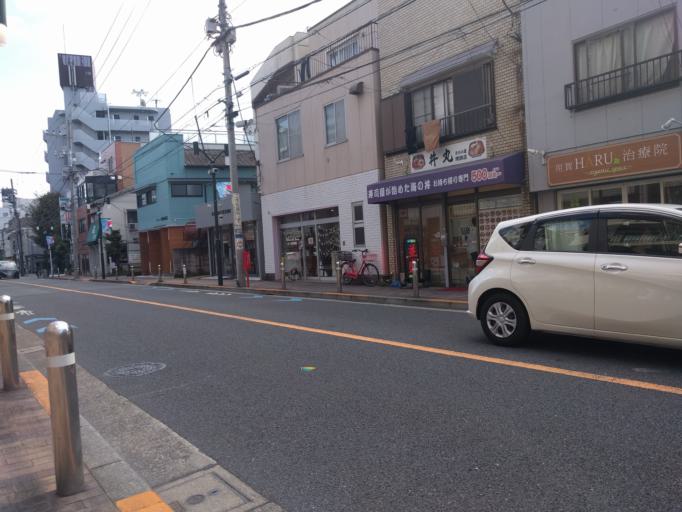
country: JP
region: Tokyo
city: Tokyo
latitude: 35.6296
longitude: 139.6343
